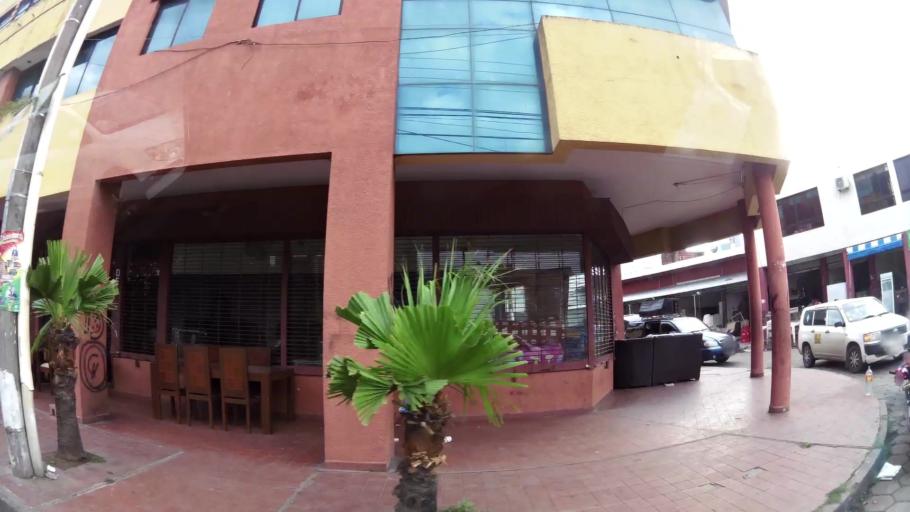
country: BO
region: Santa Cruz
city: Santa Cruz de la Sierra
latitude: -17.7754
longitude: -63.1770
